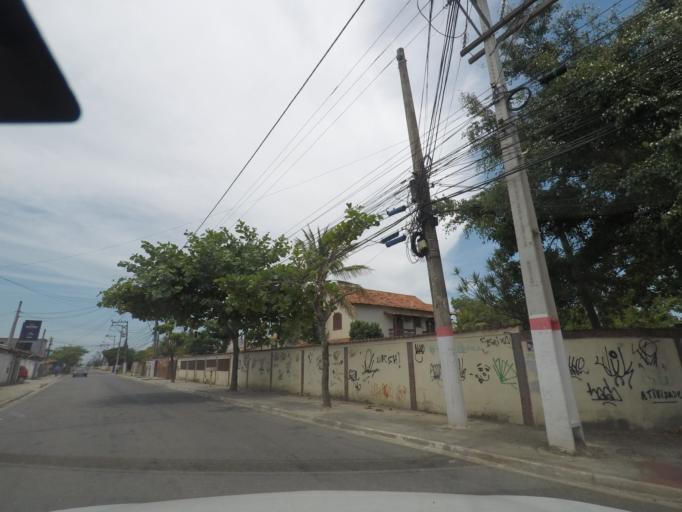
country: BR
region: Rio de Janeiro
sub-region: Niteroi
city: Niteroi
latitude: -22.9647
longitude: -42.9756
